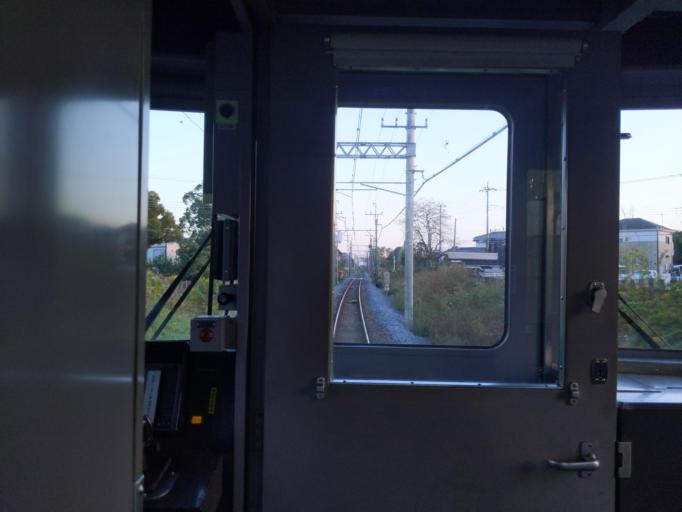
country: JP
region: Chiba
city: Noda
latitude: 35.9688
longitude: 139.8541
